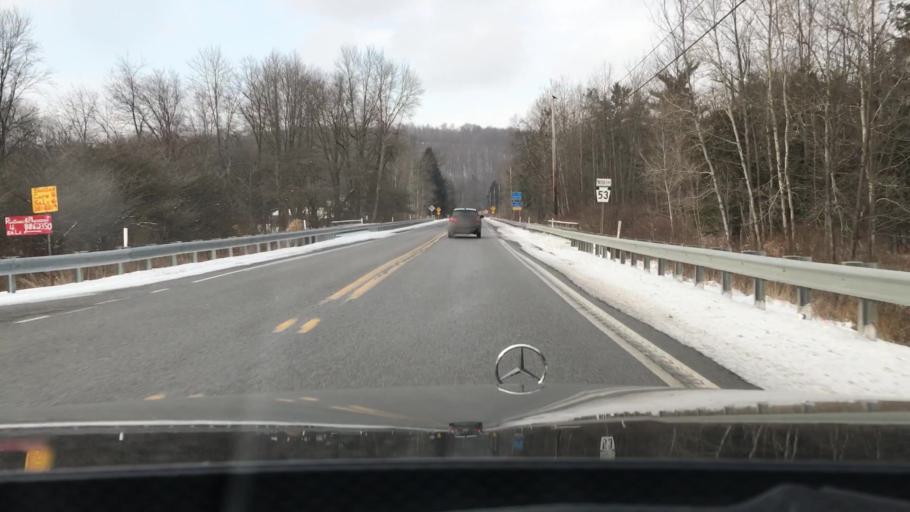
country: US
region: Pennsylvania
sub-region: Cambria County
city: Gallitzin
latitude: 40.5085
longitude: -78.5820
